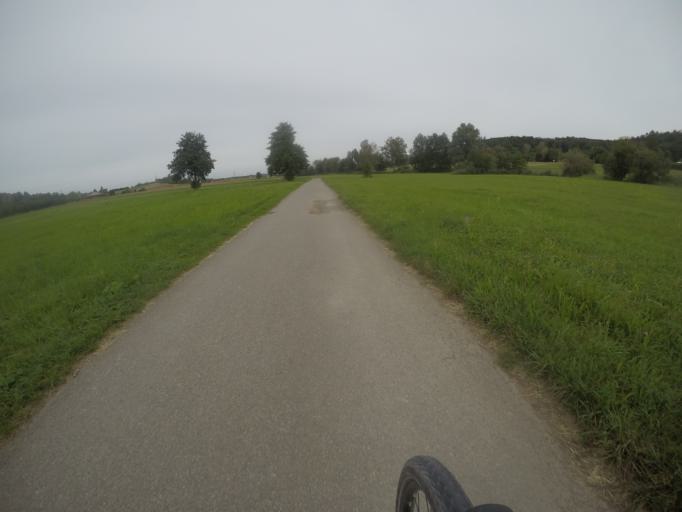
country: DE
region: Baden-Wuerttemberg
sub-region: Regierungsbezirk Stuttgart
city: Magstadt
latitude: 48.7421
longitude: 8.9897
